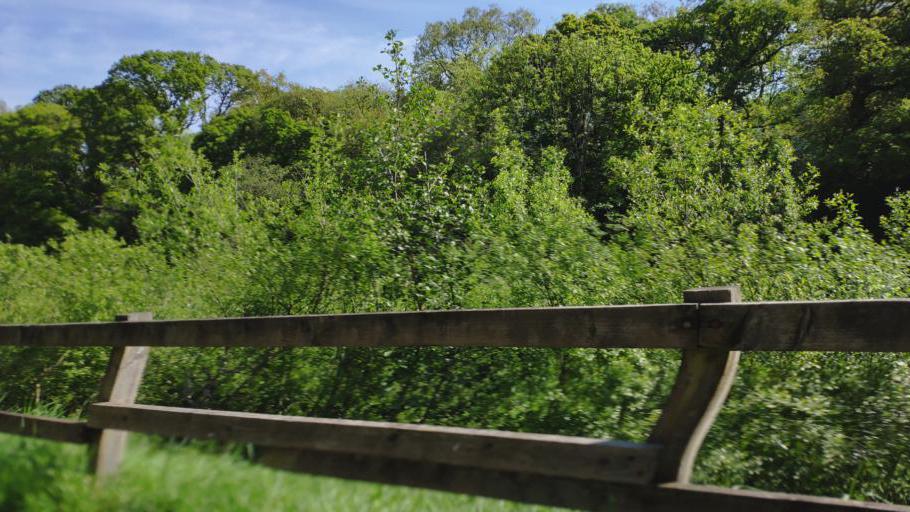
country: IE
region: Munster
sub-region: County Cork
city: Blarney
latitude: 51.9393
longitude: -8.5638
